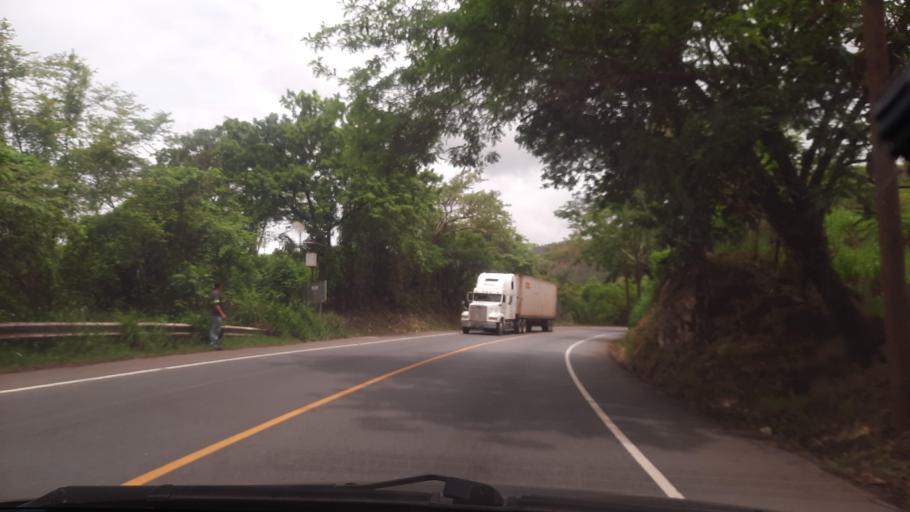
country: GT
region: Izabal
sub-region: Municipio de Los Amates
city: Los Amates
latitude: 15.2323
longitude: -89.1972
